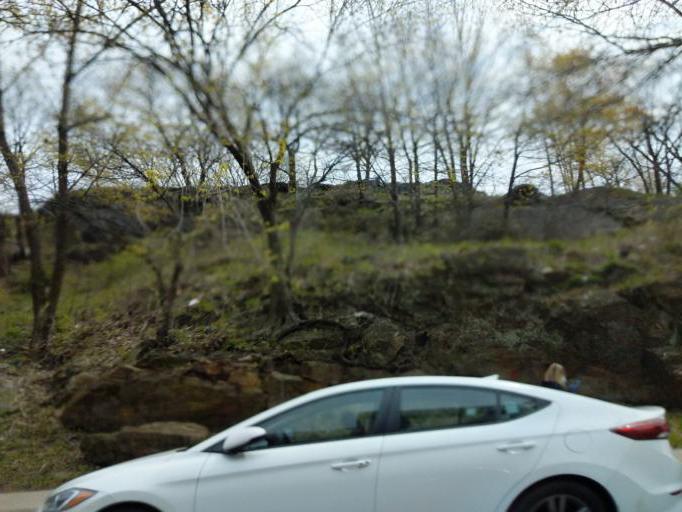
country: US
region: New York
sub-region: Bronx
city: The Bronx
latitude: 40.8455
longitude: -73.8967
